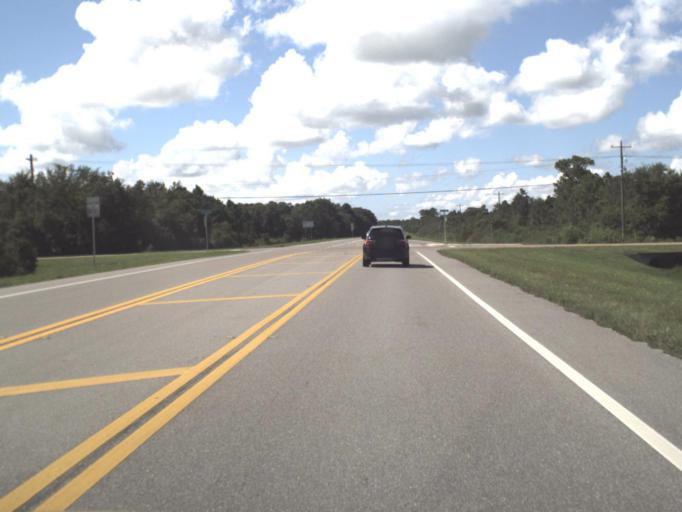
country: US
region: Florida
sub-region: Sarasota County
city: Fruitville
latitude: 27.3986
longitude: -82.3036
